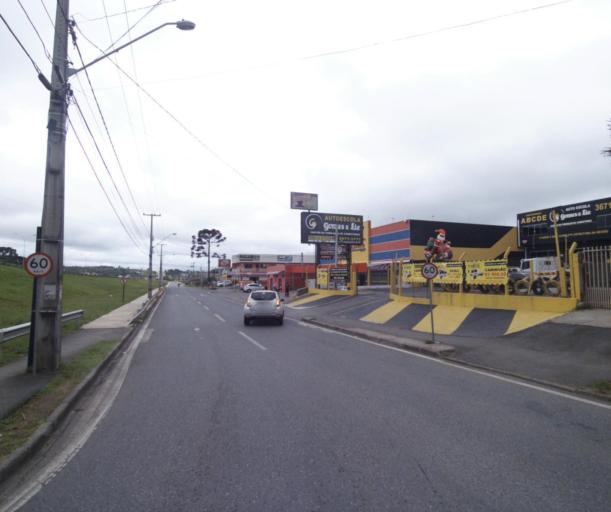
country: BR
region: Parana
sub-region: Quatro Barras
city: Quatro Barras
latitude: -25.3678
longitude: -49.1008
